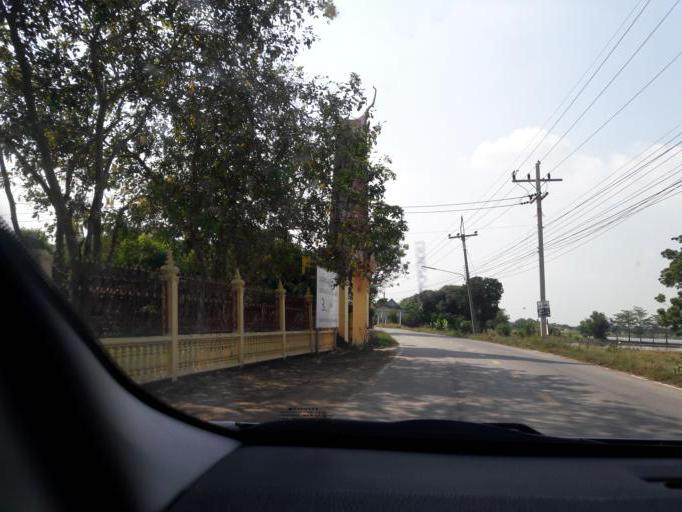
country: TH
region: Ang Thong
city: Ang Thong
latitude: 14.5436
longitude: 100.4021
